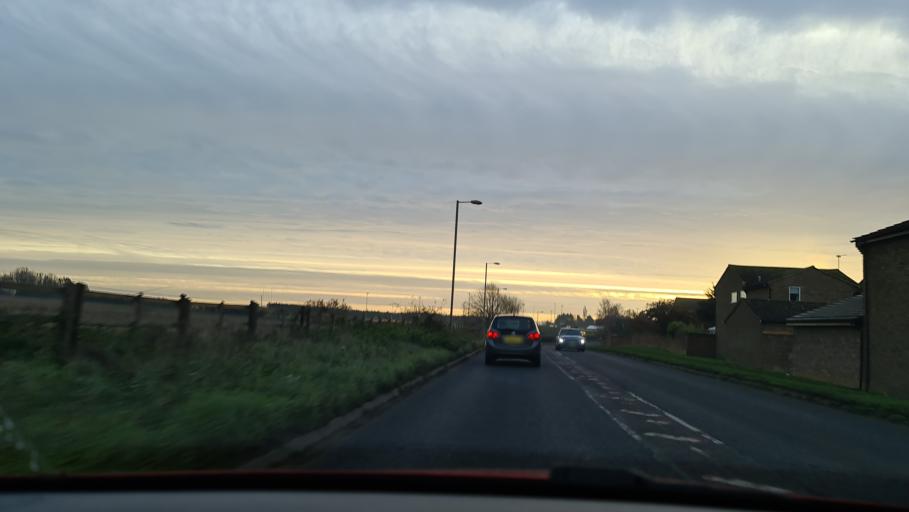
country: GB
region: England
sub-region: Oxfordshire
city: Thame
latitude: 51.7506
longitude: -0.9651
